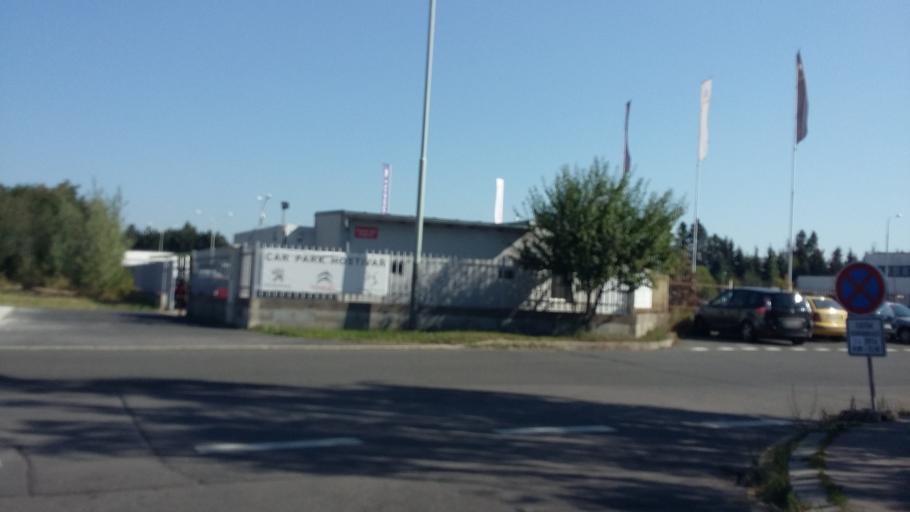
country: CZ
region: Praha
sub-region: Praha 9
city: Vysocany
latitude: 50.0590
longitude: 14.5182
